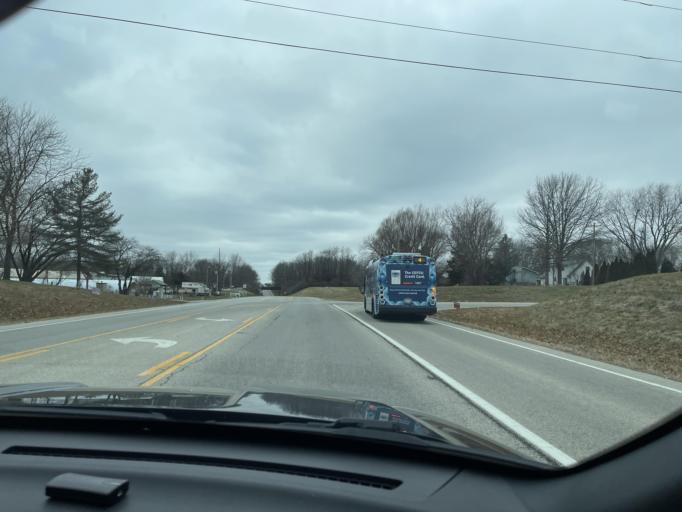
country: US
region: Illinois
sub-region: Sangamon County
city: Leland Grove
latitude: 39.8177
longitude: -89.7067
